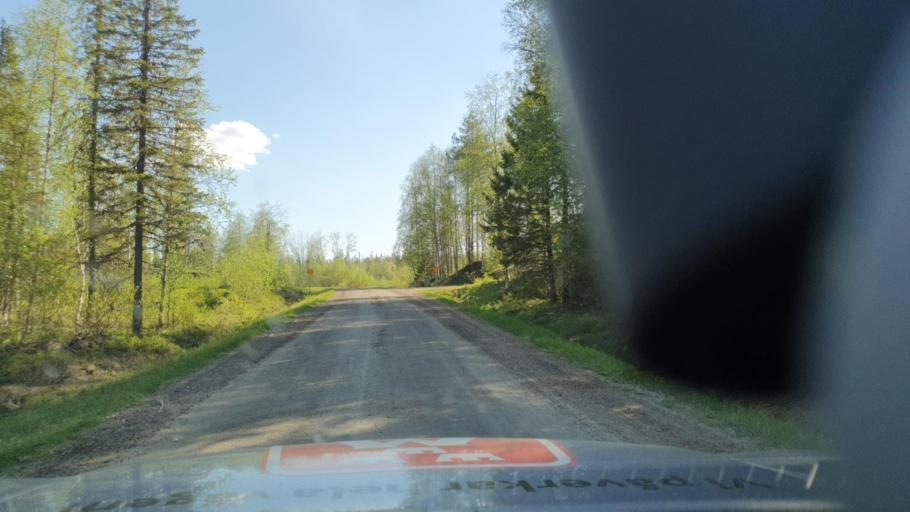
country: SE
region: Norrbotten
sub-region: Bodens Kommun
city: Boden
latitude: 66.5222
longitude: 21.9032
